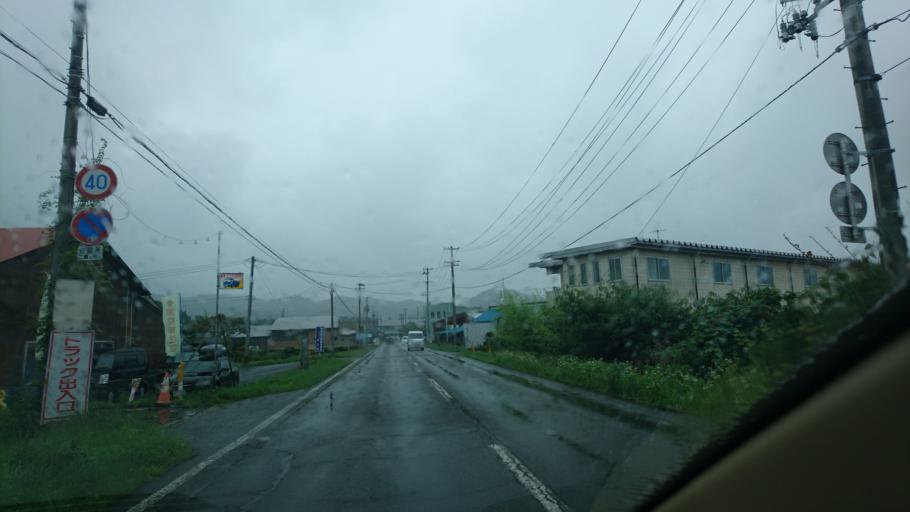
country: JP
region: Iwate
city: Kitakami
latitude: 39.2724
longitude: 141.1139
